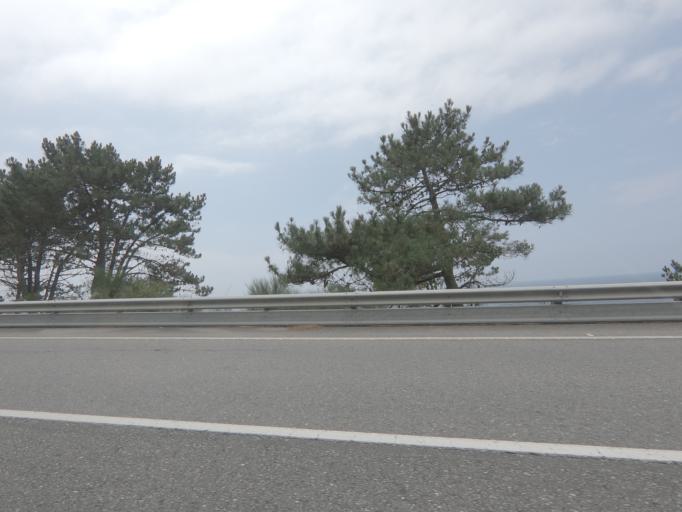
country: ES
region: Galicia
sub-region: Provincia de Pontevedra
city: Oia
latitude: 41.9549
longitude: -8.8834
